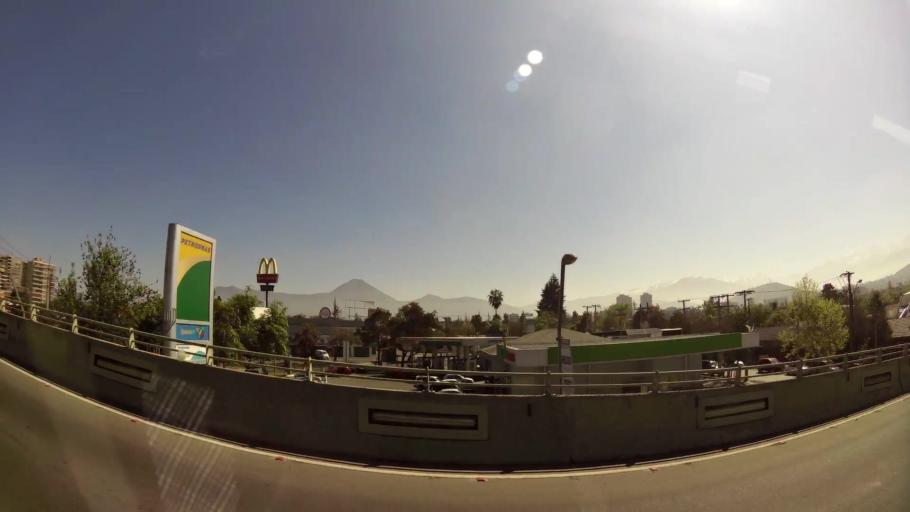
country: CL
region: Santiago Metropolitan
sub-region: Provincia de Santiago
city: Villa Presidente Frei, Nunoa, Santiago, Chile
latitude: -33.4181
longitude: -70.5523
